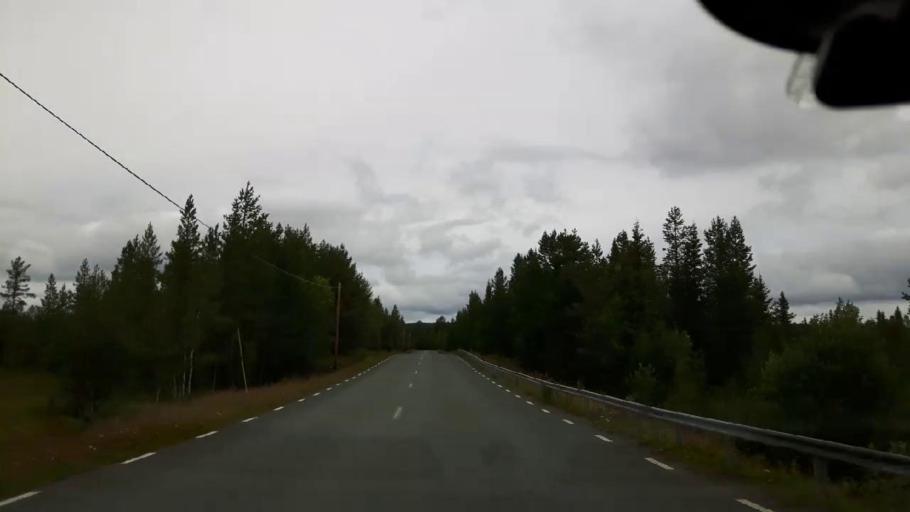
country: SE
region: Jaemtland
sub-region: Krokoms Kommun
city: Valla
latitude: 63.6757
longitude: 13.8695
